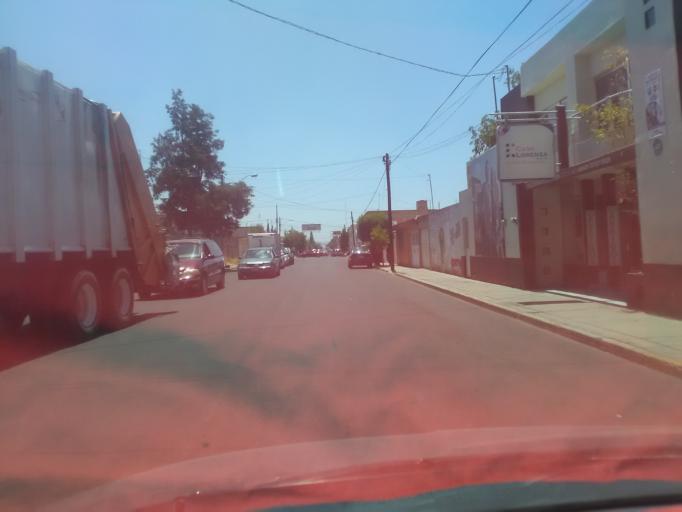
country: MX
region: Durango
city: Victoria de Durango
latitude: 24.0129
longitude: -104.6823
